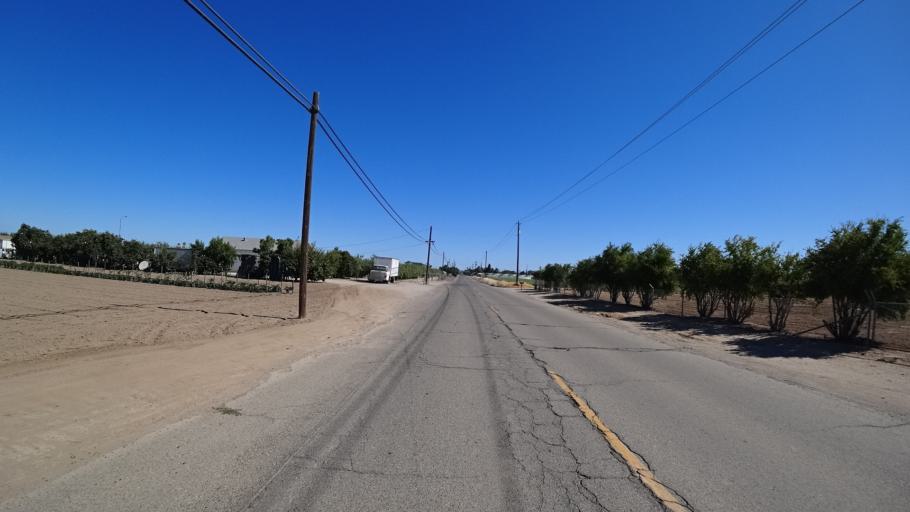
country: US
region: California
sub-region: Fresno County
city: West Park
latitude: 36.7025
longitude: -119.8089
